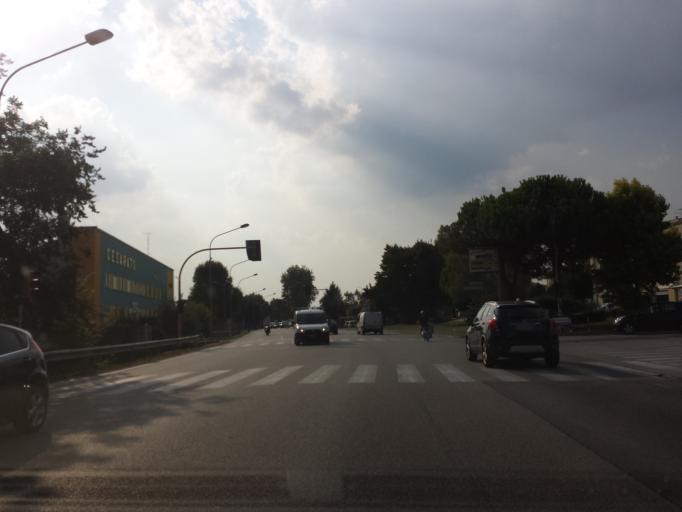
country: IT
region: Veneto
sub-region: Provincia di Padova
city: Sarmeola
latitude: 45.4202
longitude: 11.8176
